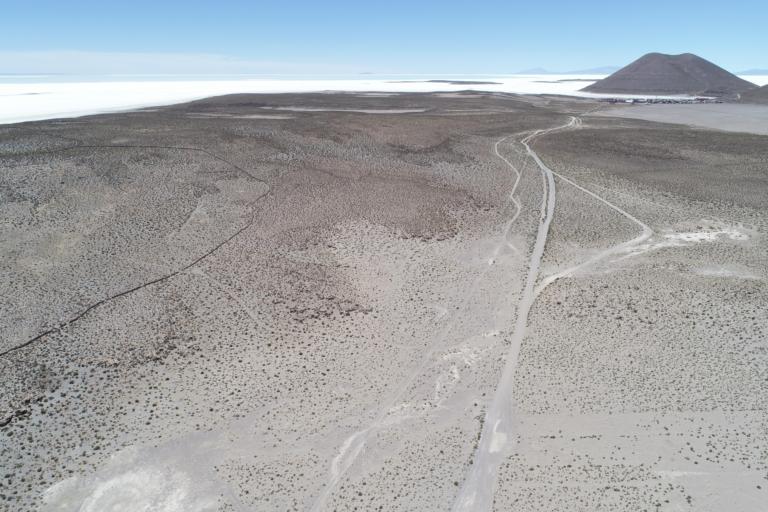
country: BO
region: Oruro
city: Cruz de Machacamarca
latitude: -19.2621
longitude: -68.3032
